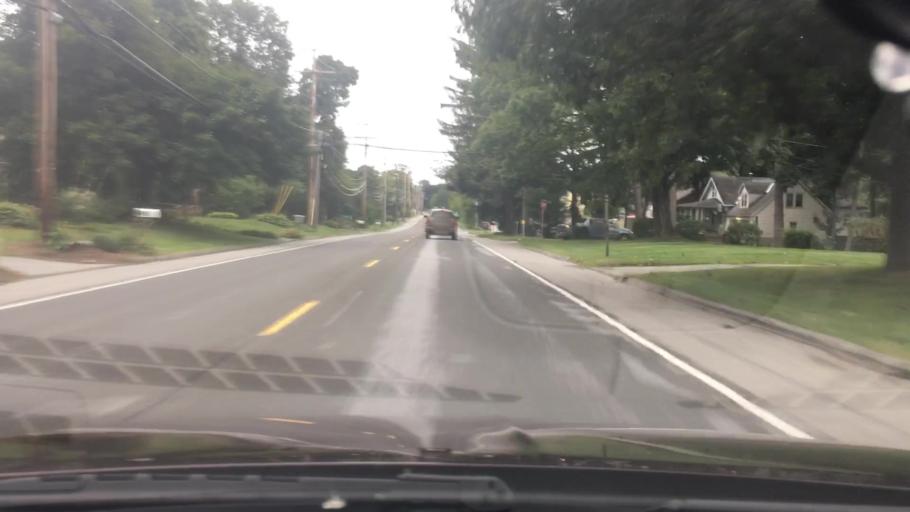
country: US
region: New York
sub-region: Dutchess County
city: Arlington
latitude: 41.7125
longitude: -73.8630
